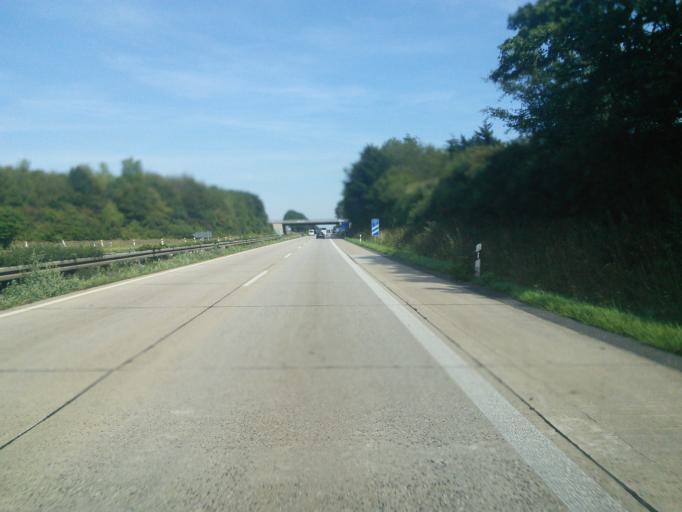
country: DE
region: North Rhine-Westphalia
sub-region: Regierungsbezirk Dusseldorf
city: Viersen
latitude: 51.2112
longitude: 6.3416
